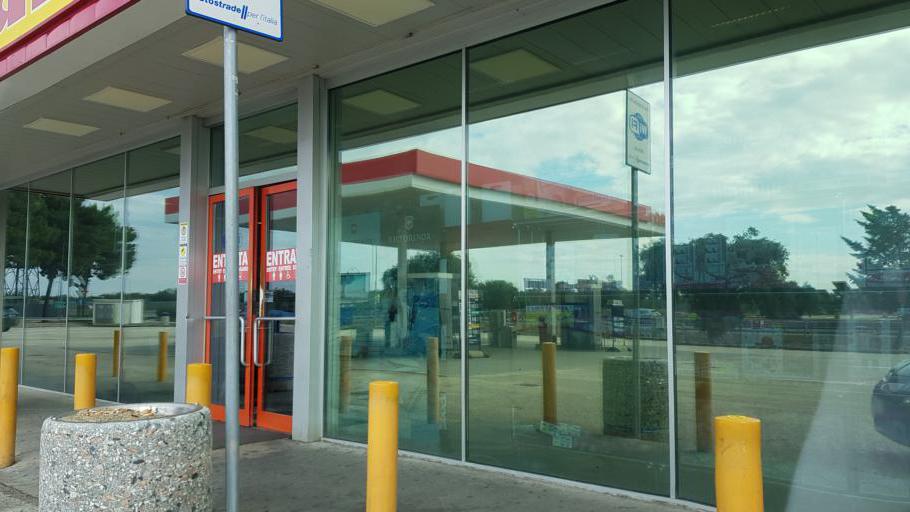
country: IT
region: Apulia
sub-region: Provincia di Barletta - Andria - Trani
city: Bisceglie
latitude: 41.1940
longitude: 16.4810
